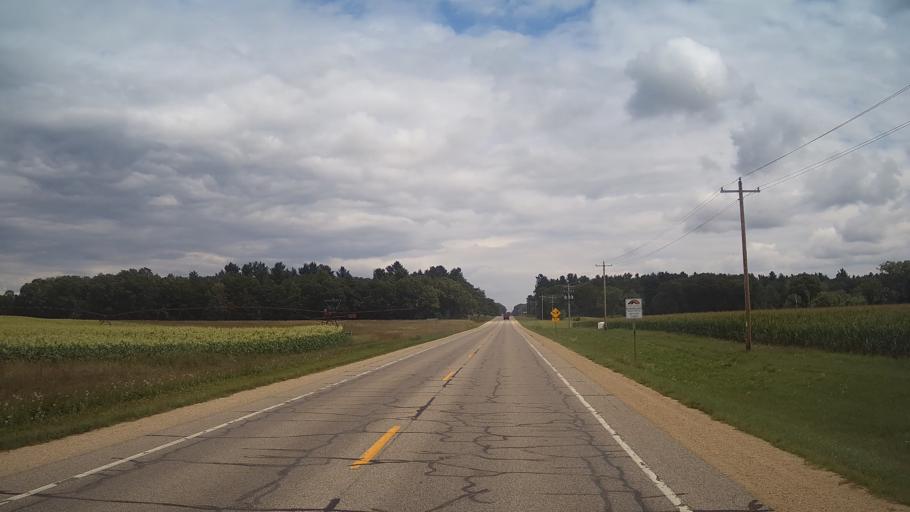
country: US
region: Wisconsin
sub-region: Waushara County
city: Wautoma
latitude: 44.0684
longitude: -89.3365
